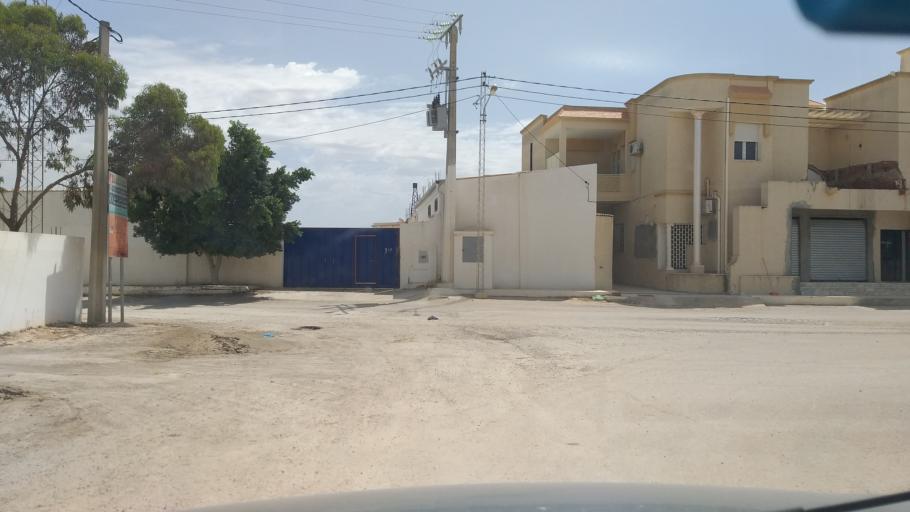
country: TN
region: Al Mahdiyah
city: El Jem
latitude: 35.3067
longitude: 10.7037
